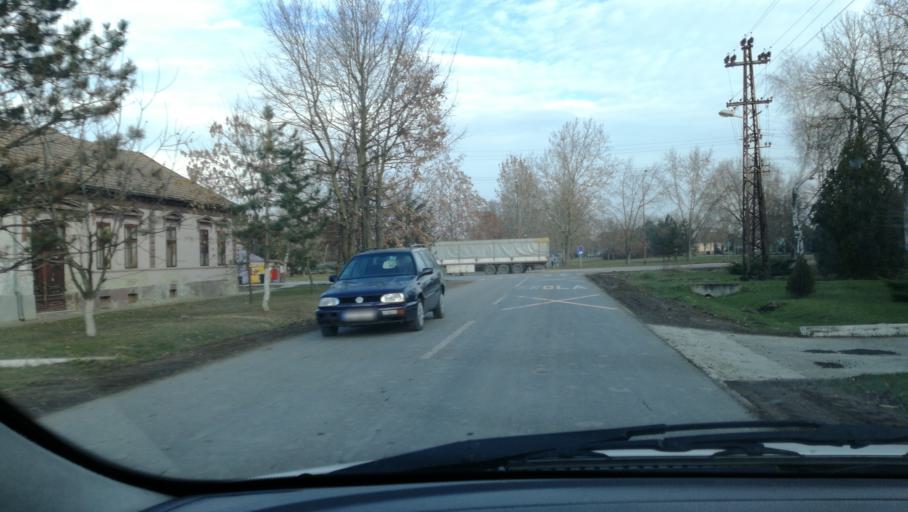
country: RS
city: Novi Kozarci
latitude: 45.7815
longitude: 20.6223
